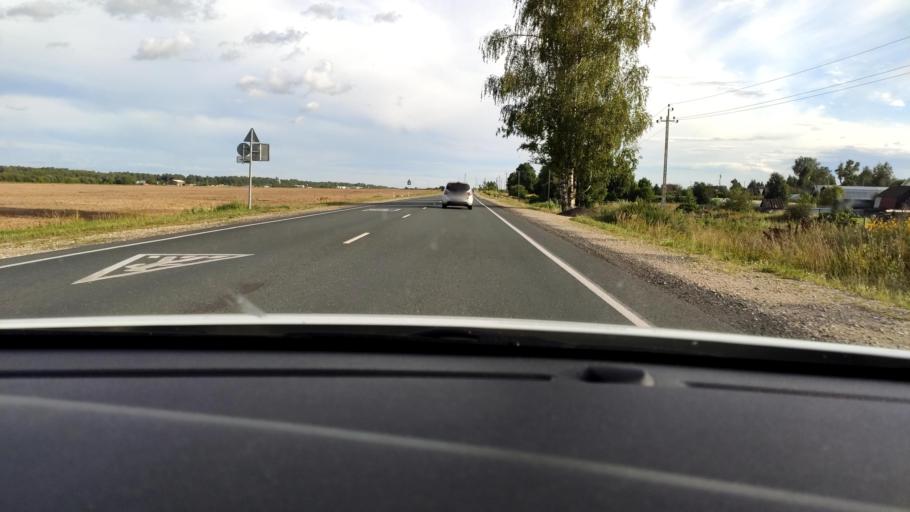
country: RU
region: Mariy-El
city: Suslonger
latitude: 56.2232
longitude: 48.2350
